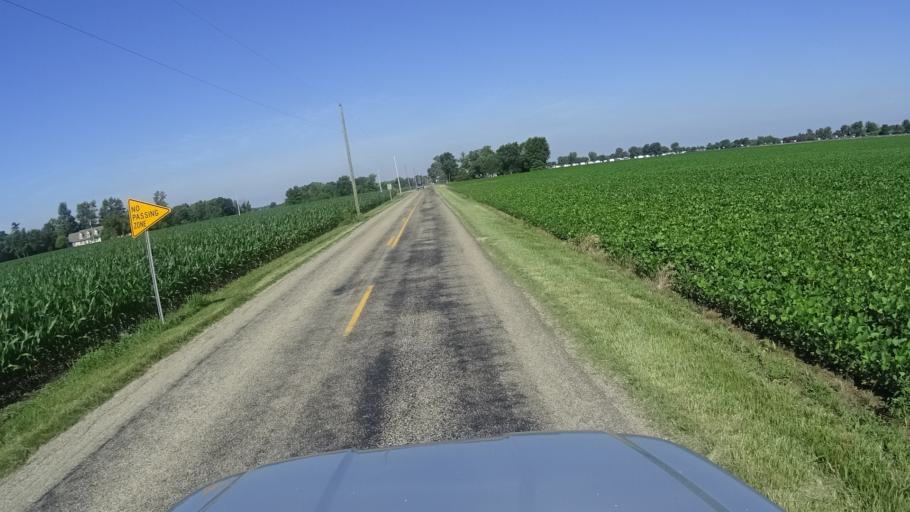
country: US
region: Indiana
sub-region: Madison County
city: Ingalls
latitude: 39.9878
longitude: -85.8221
